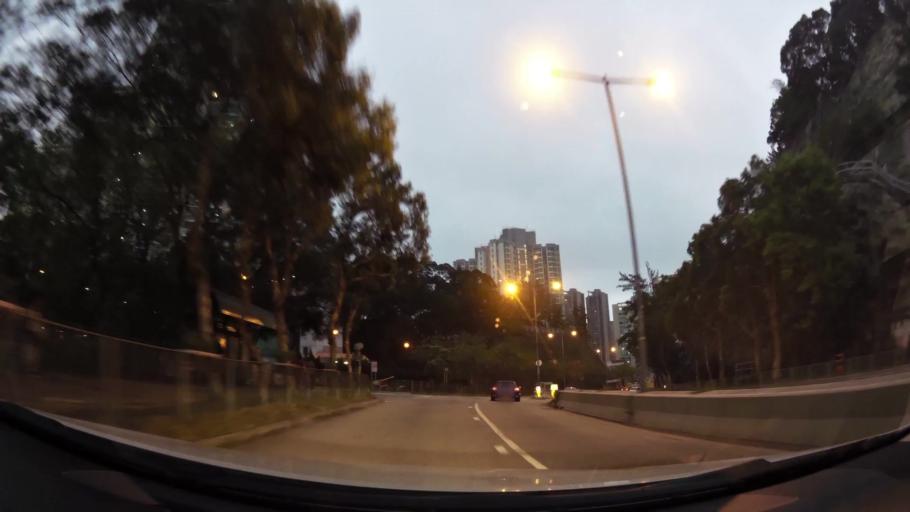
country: HK
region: Tsuen Wan
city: Tsuen Wan
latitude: 22.3479
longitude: 114.1075
